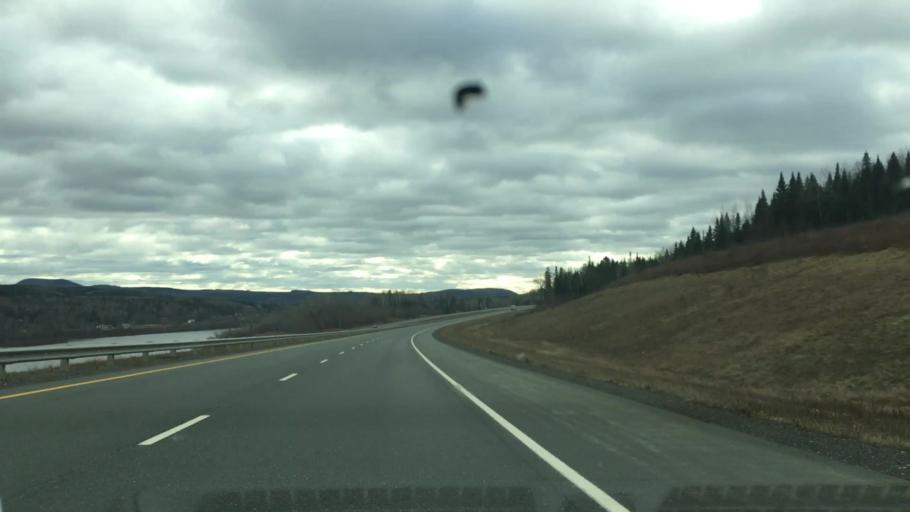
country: US
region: Maine
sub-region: Aroostook County
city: Fort Fairfield
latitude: 46.6799
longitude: -67.7314
